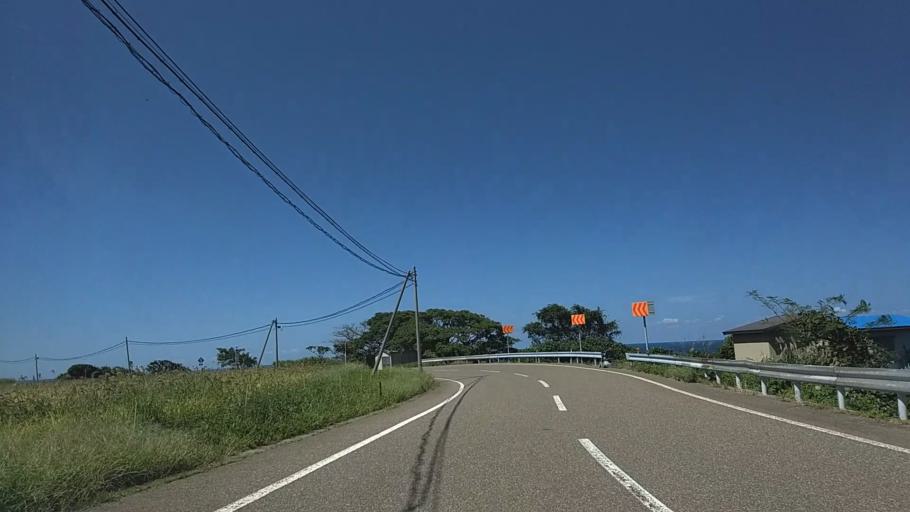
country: JP
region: Niigata
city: Joetsu
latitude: 37.1723
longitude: 138.0994
